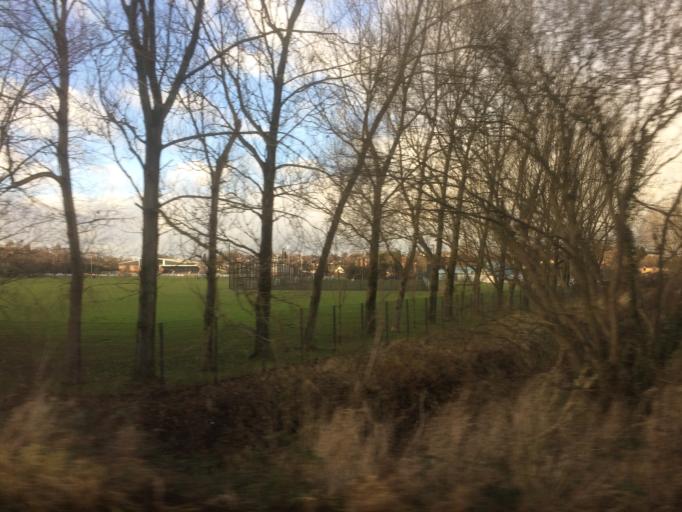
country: GB
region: Scotland
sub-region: East Renfrewshire
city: Giffnock
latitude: 55.8081
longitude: -4.2752
